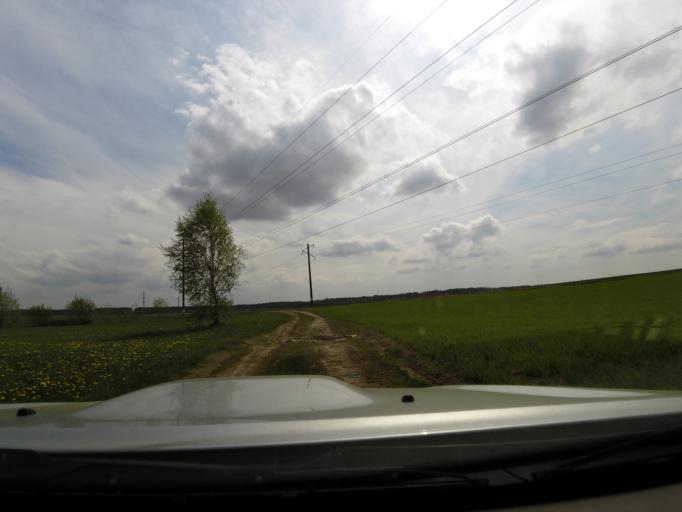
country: LT
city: Salcininkai
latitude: 54.4171
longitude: 25.3118
